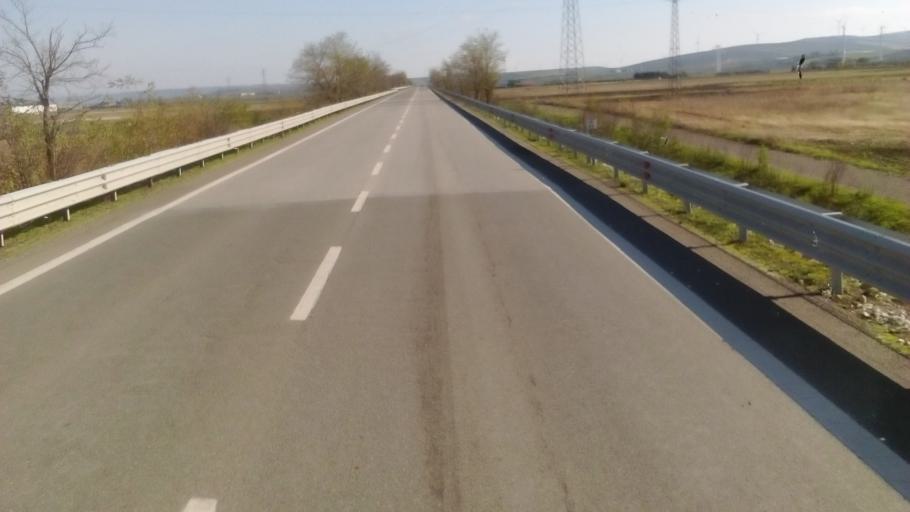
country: IT
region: Basilicate
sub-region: Provincia di Potenza
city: Zona 179
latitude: 41.0781
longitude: 15.6350
